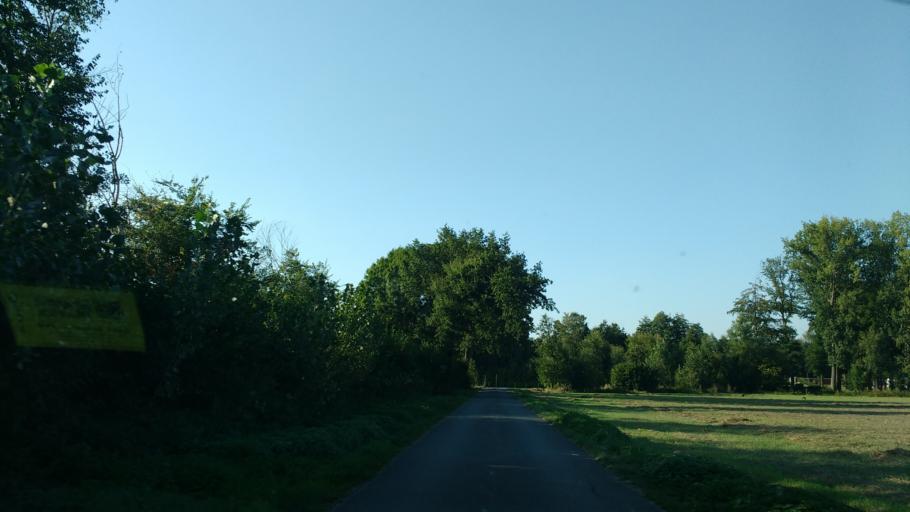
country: DE
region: North Rhine-Westphalia
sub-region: Regierungsbezirk Detmold
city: Delbruck
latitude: 51.7579
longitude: 8.5391
